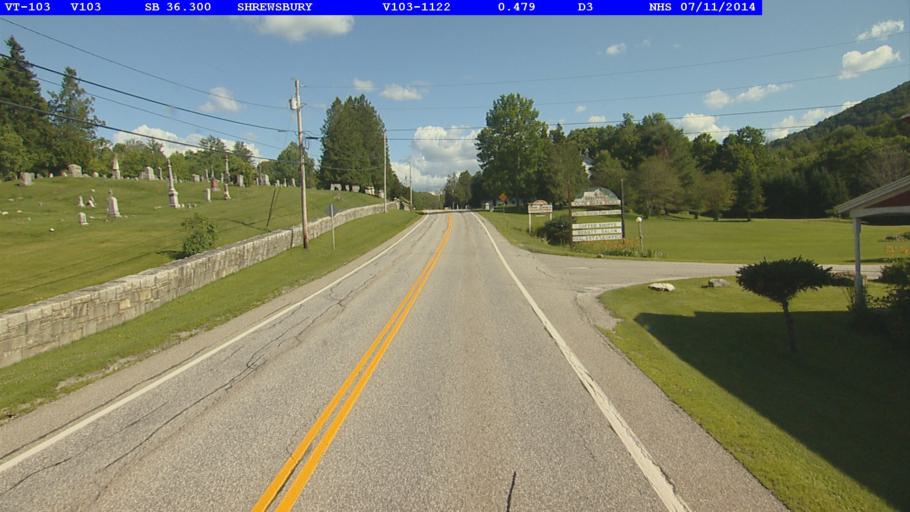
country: US
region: Vermont
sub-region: Rutland County
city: Rutland
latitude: 43.4862
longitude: -72.8800
